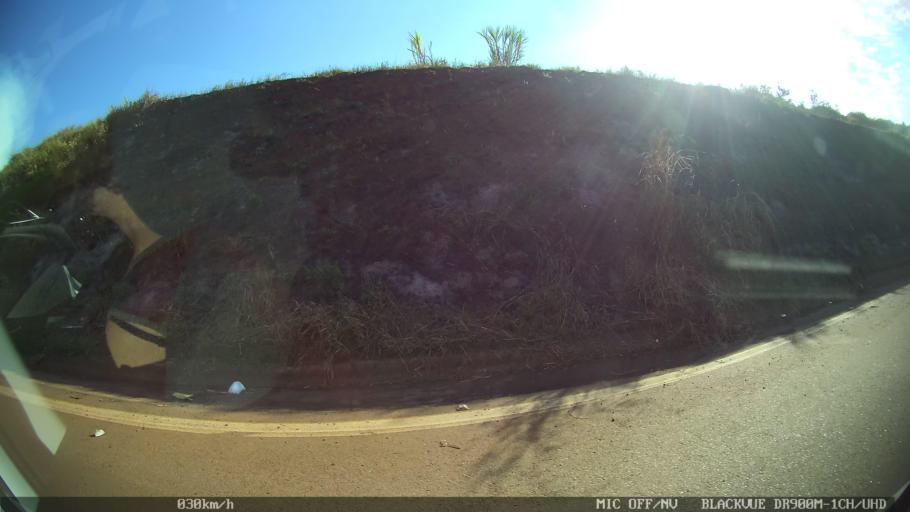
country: BR
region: Sao Paulo
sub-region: Piracicaba
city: Piracicaba
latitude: -22.6916
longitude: -47.6012
